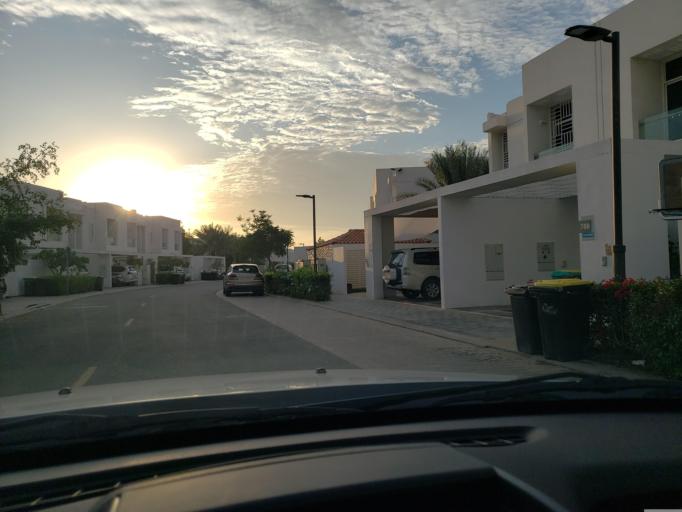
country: AE
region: Dubai
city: Dubai
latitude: 25.0196
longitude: 55.2736
